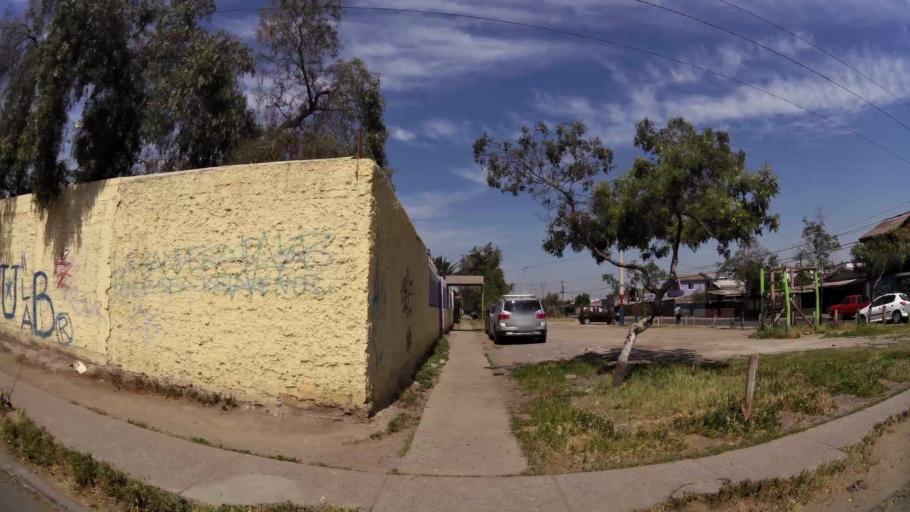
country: CL
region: Santiago Metropolitan
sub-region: Provincia de Santiago
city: La Pintana
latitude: -33.5476
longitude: -70.6455
